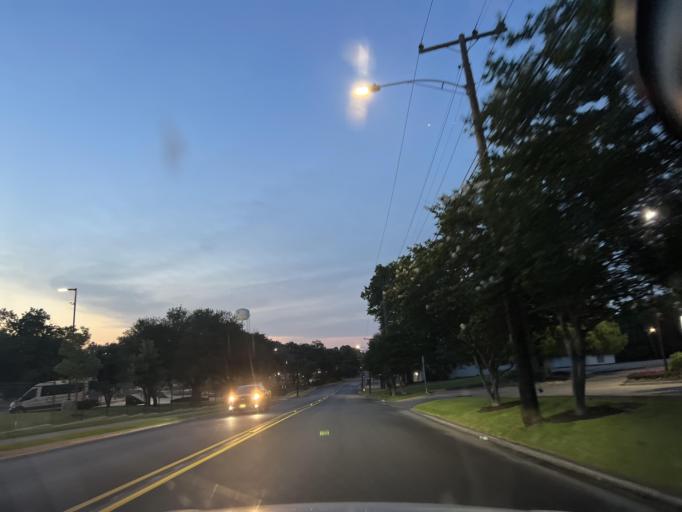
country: US
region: Texas
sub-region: Washington County
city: Brenham
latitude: 30.1710
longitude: -96.3992
